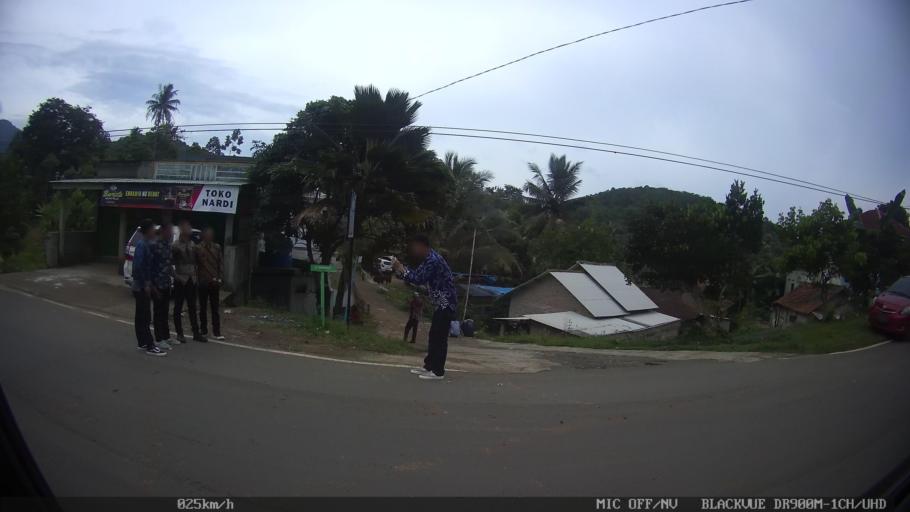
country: ID
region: Lampung
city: Bandarlampung
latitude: -5.4149
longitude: 105.1899
